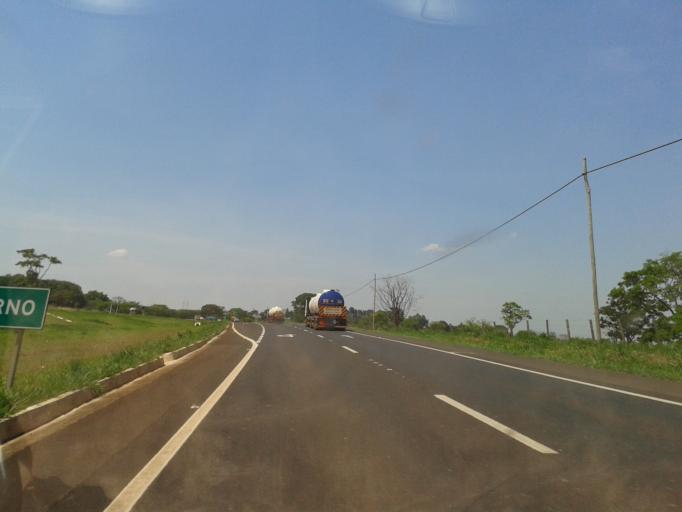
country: BR
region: Minas Gerais
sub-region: Monte Alegre De Minas
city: Monte Alegre de Minas
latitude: -18.8736
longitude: -48.5997
